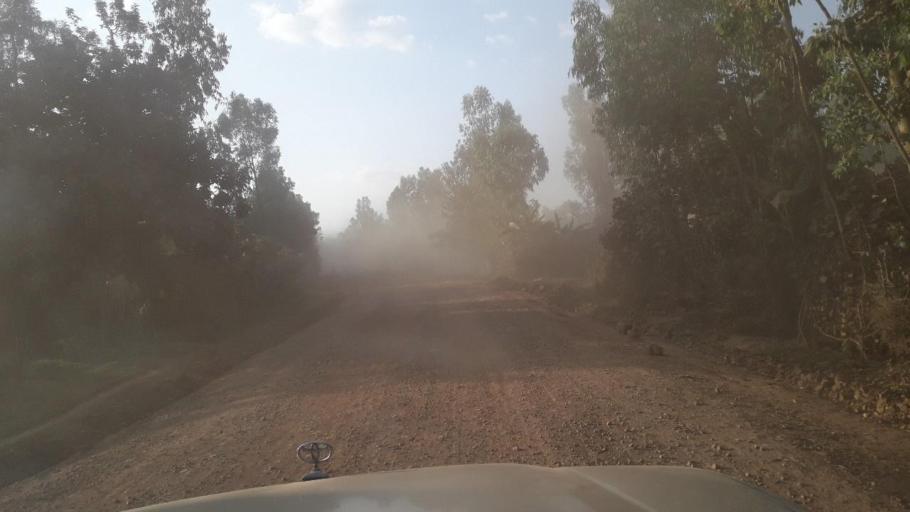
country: ET
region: Oromiya
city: Jima
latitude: 7.6223
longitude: 36.8341
